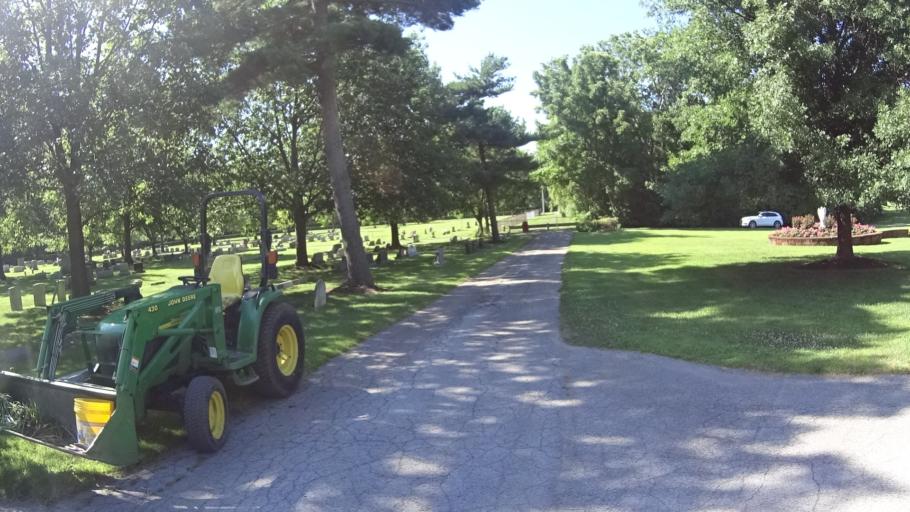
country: US
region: Ohio
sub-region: Erie County
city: Sandusky
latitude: 41.3996
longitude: -82.6517
